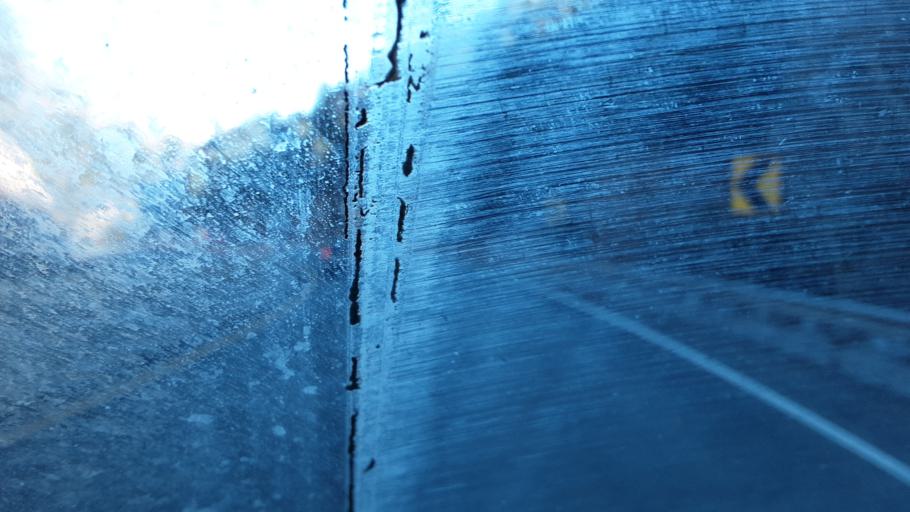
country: US
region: Colorado
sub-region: Jefferson County
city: Indian Hills
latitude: 39.6180
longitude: -105.2243
